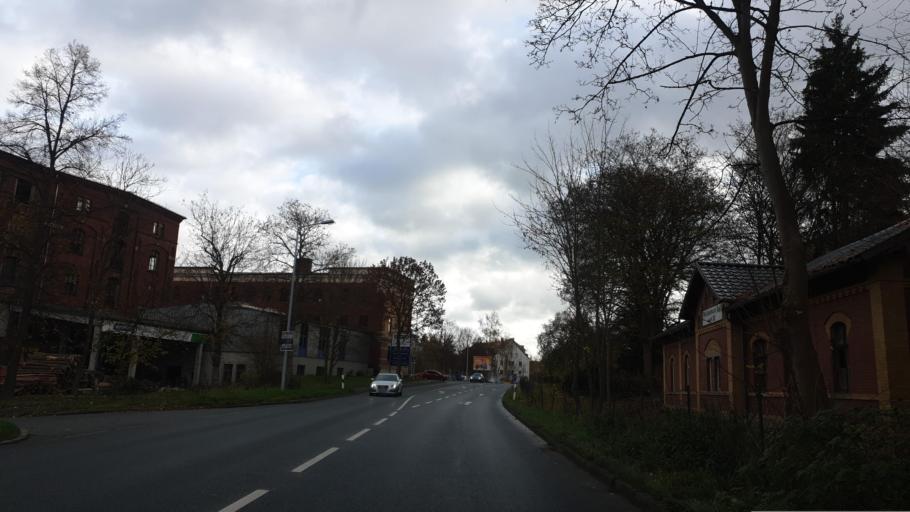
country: DE
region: Saxony
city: Reichenbach/Vogtland
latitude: 50.6190
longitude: 12.2995
